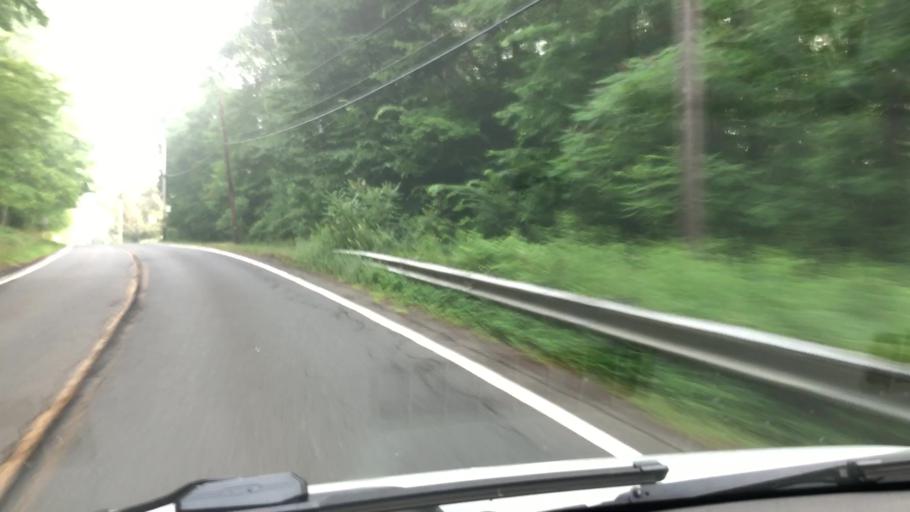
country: US
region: Massachusetts
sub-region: Hampshire County
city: Chesterfield
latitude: 42.4315
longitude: -72.7898
